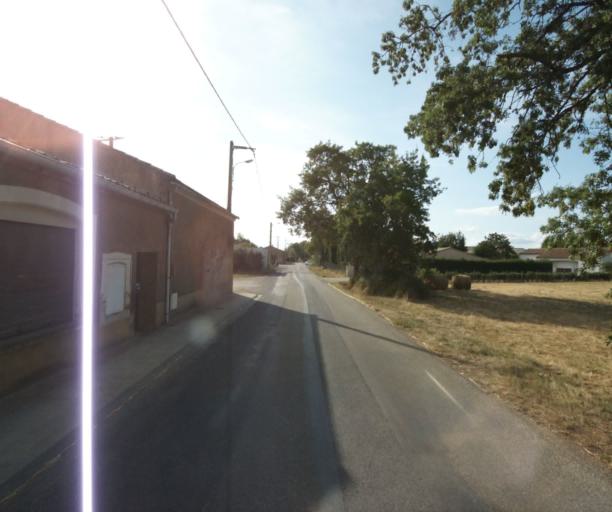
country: FR
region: Midi-Pyrenees
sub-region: Departement de la Haute-Garonne
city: Revel
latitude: 43.4667
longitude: 2.0053
